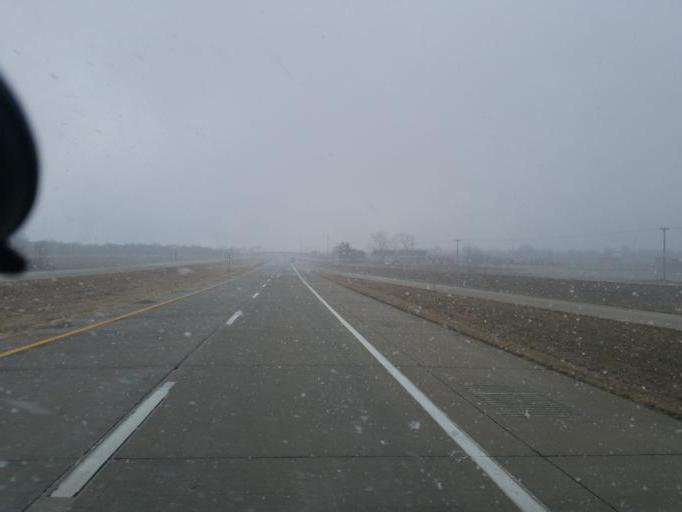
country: US
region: Missouri
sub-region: Randolph County
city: Moberly
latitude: 39.4414
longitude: -92.4232
